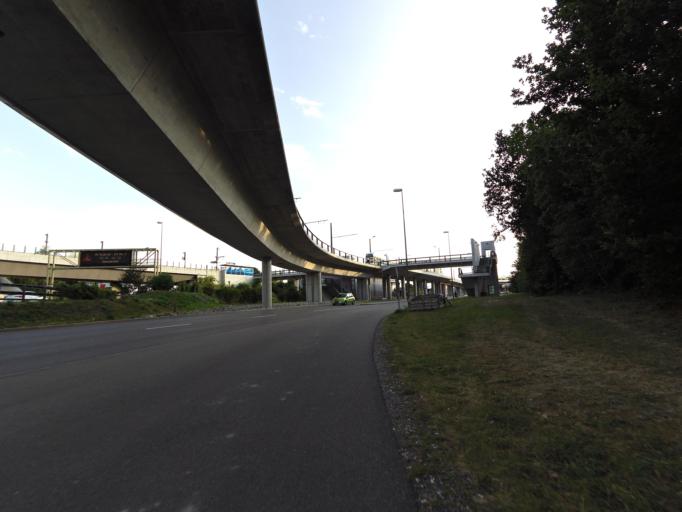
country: CH
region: Zurich
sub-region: Bezirk Buelach
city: Kloten / Balsberg
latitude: 47.4424
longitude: 8.5694
